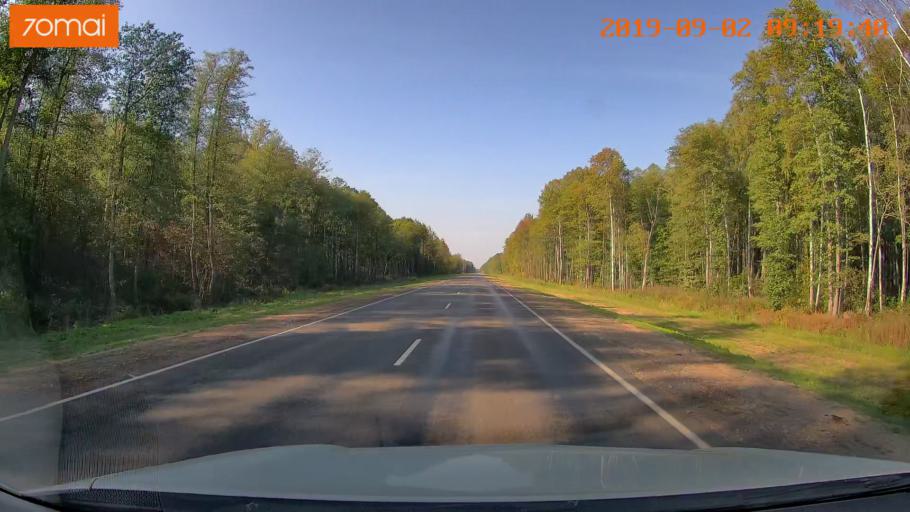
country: RU
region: Kaluga
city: Yukhnov
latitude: 54.8069
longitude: 35.4020
